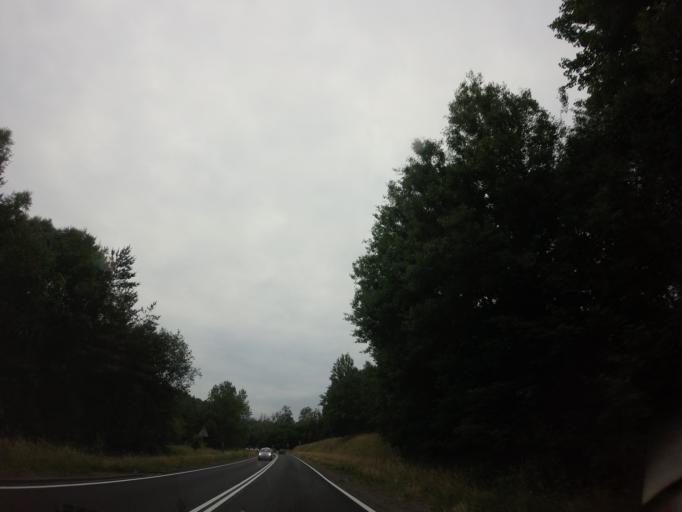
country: PL
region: West Pomeranian Voivodeship
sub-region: Powiat walecki
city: Miroslawiec
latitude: 53.3316
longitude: 16.0293
